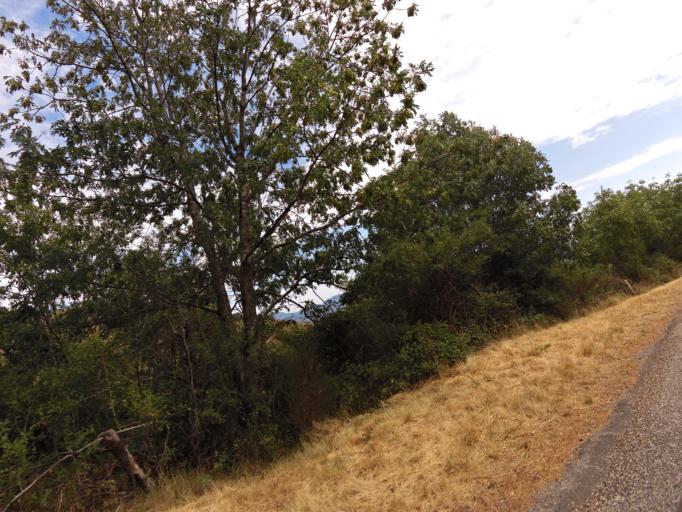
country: FR
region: Languedoc-Roussillon
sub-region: Departement du Gard
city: Le Vigan
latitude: 44.0382
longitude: 3.6067
